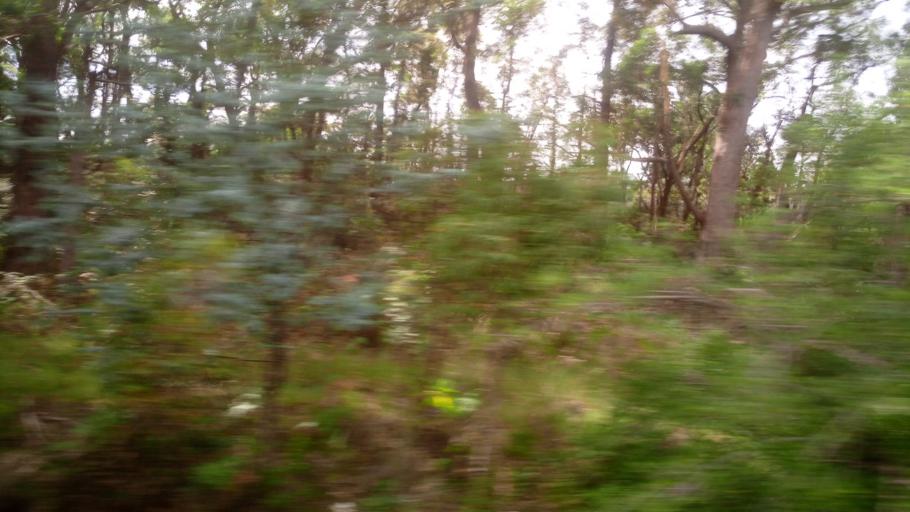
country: AU
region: New South Wales
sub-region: Blue Mountains Municipality
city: Lawson
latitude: -33.7237
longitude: 150.4044
